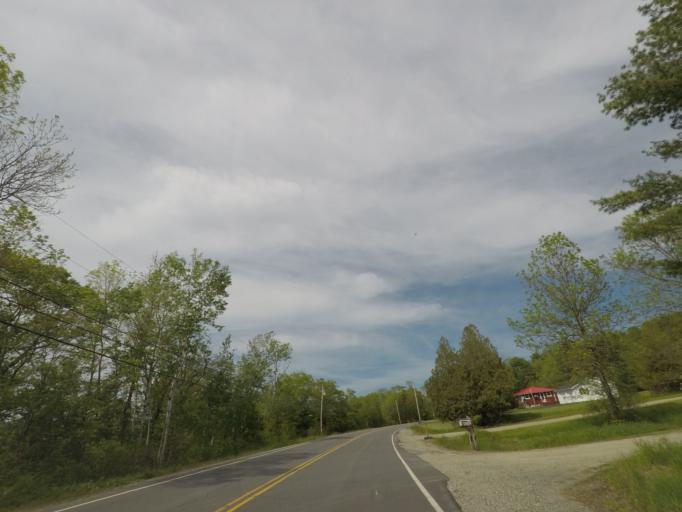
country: US
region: Maine
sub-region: Sagadahoc County
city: Richmond
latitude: 44.0943
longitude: -69.7425
